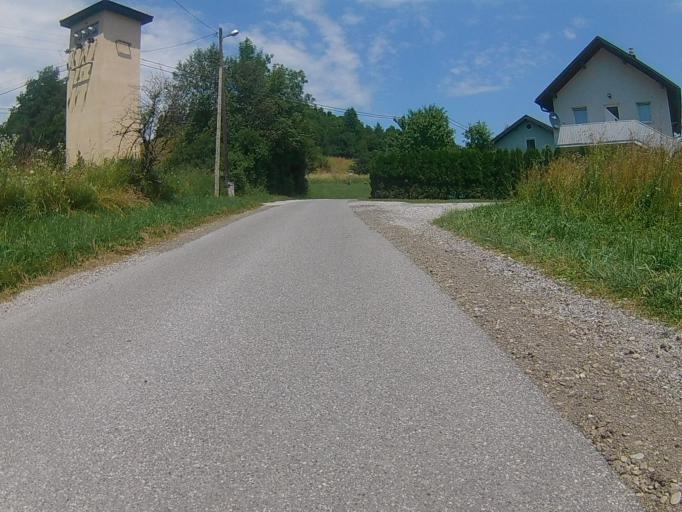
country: SI
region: Maribor
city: Kamnica
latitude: 46.5837
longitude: 15.6194
